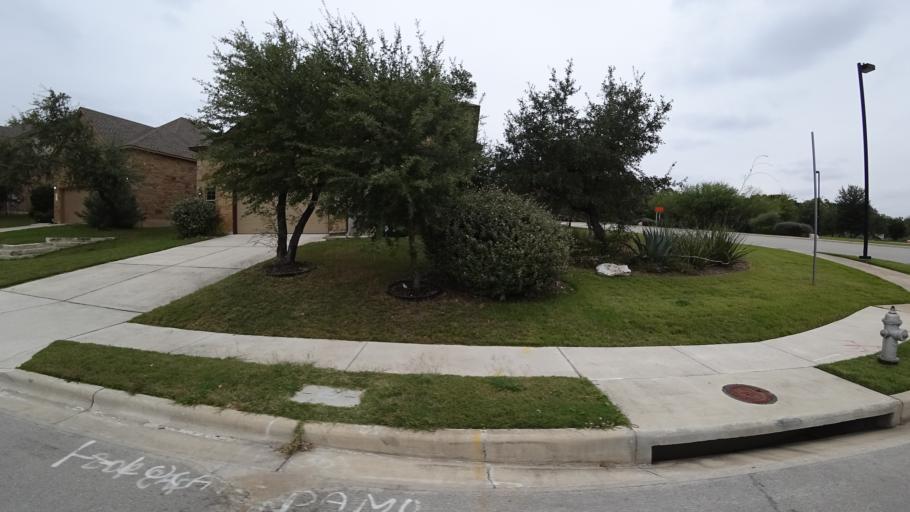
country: US
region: Texas
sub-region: Travis County
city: Shady Hollow
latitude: 30.1803
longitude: -97.9010
